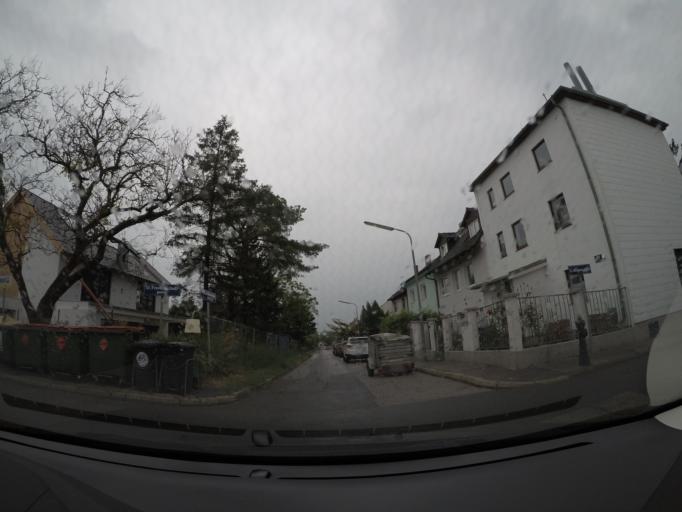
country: AT
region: Lower Austria
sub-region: Politischer Bezirk Modling
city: Perchtoldsdorf
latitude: 48.1689
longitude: 16.2648
